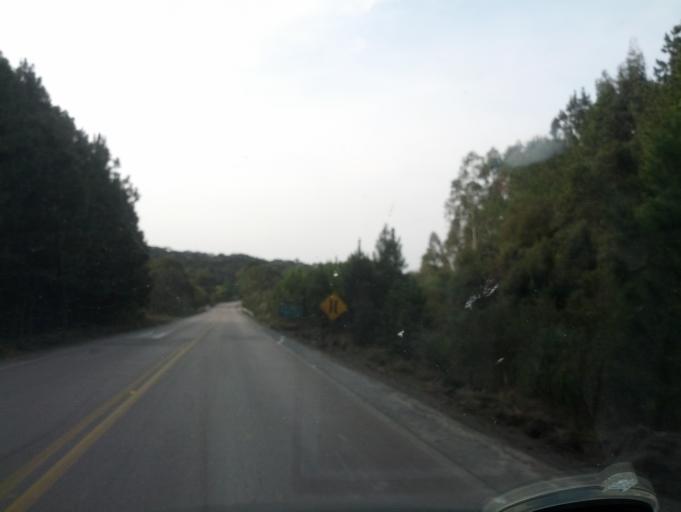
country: BR
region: Santa Catarina
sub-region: Otacilio Costa
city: Otacilio Costa
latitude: -27.3655
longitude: -50.1347
